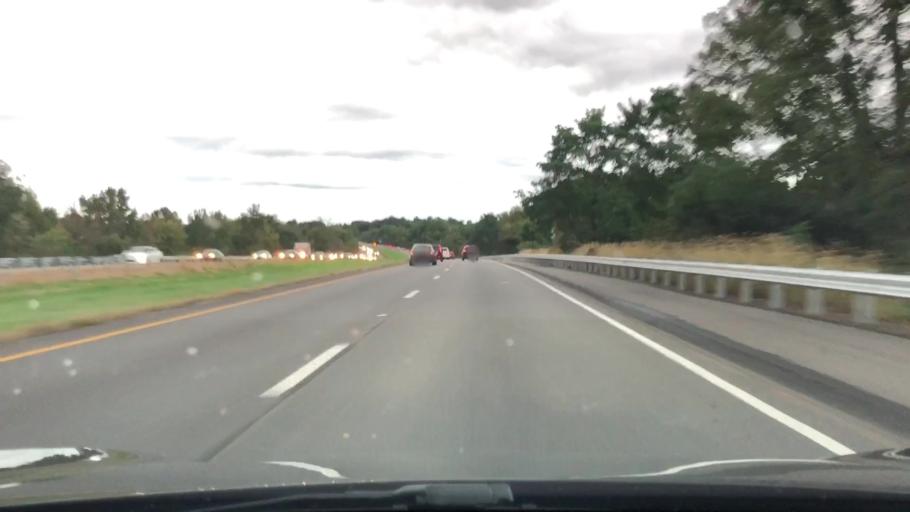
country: US
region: Pennsylvania
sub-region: Bucks County
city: Woodside
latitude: 40.2047
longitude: -74.8749
